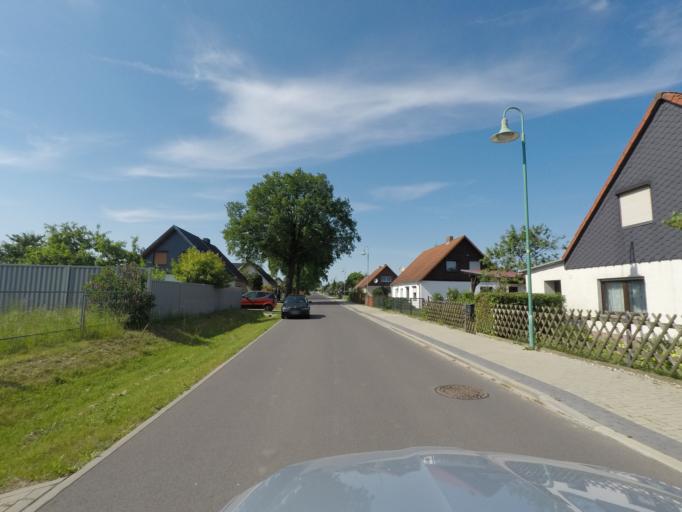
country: DE
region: Brandenburg
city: Melchow
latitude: 52.8619
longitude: 13.7257
